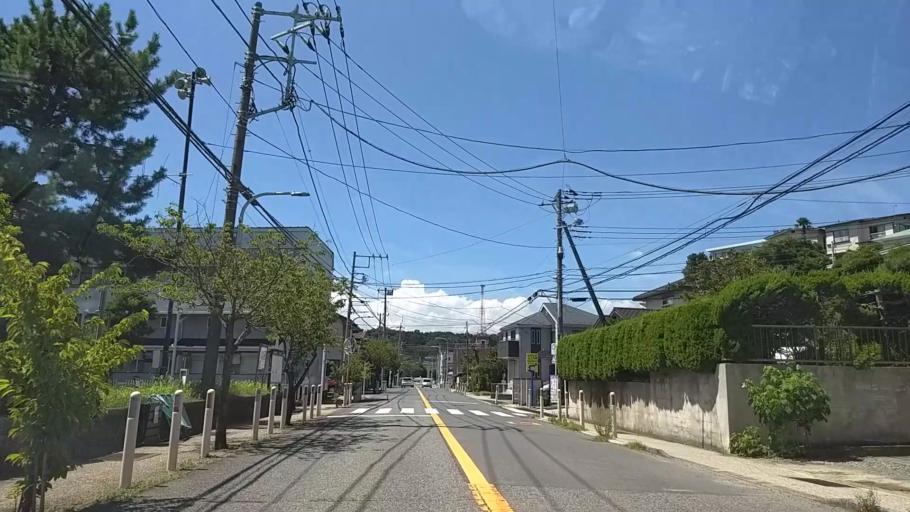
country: JP
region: Kanagawa
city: Zushi
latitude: 35.3018
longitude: 139.5928
